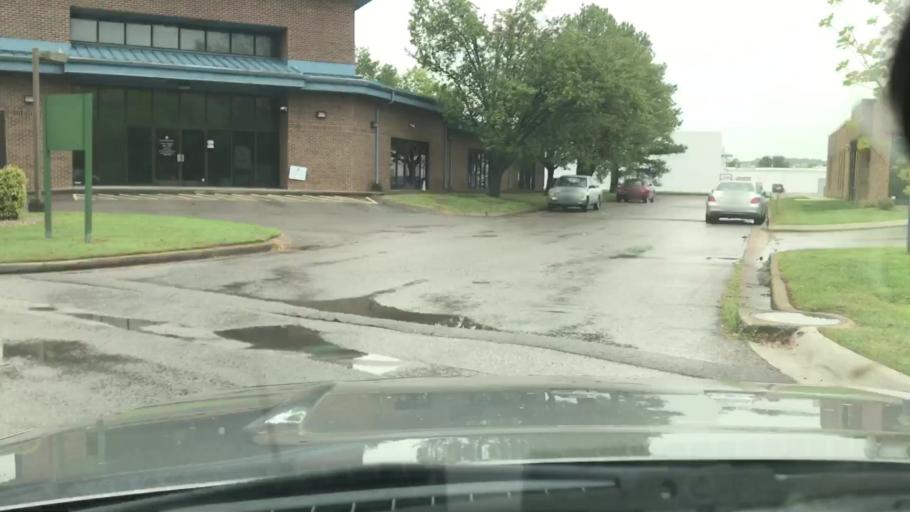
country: US
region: Tennessee
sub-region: Davidson County
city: Nashville
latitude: 36.1945
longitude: -86.7952
